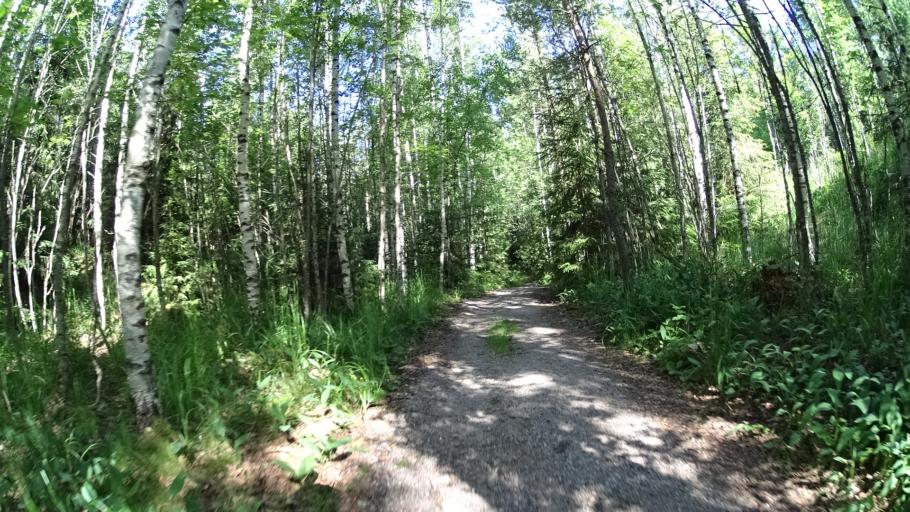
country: FI
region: Uusimaa
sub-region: Helsinki
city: Espoo
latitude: 60.3143
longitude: 24.5076
